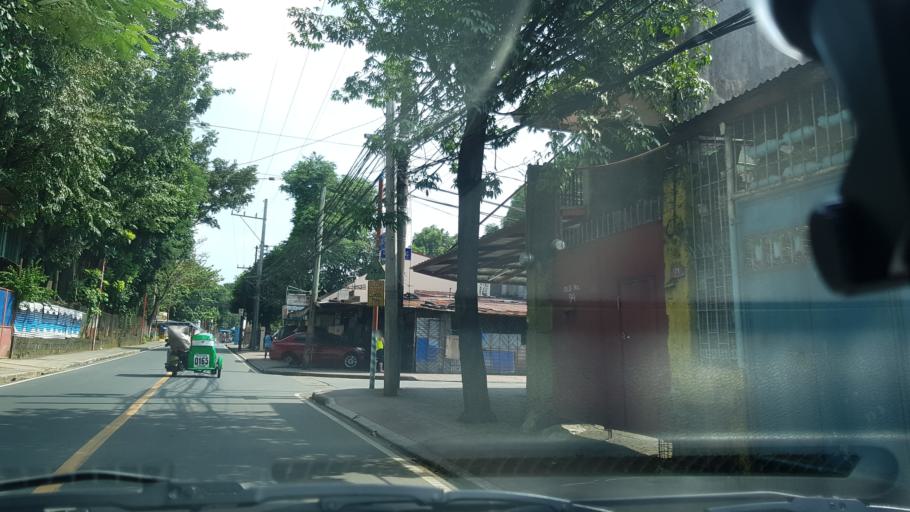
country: PH
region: Calabarzon
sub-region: Province of Rizal
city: San Mateo
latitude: 14.6638
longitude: 121.1118
